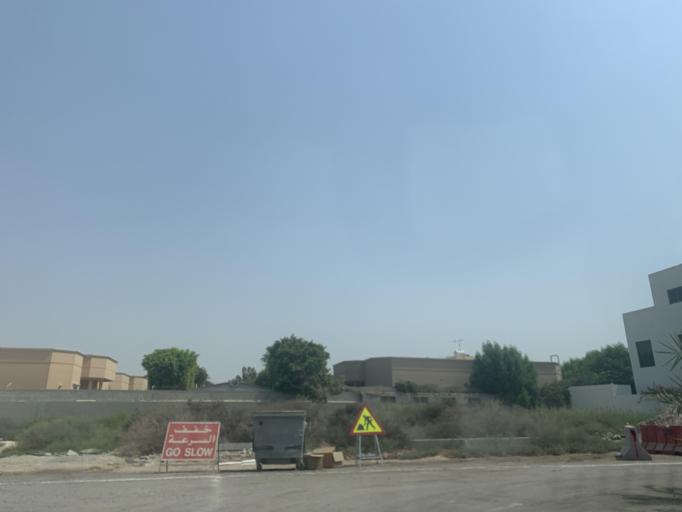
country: BH
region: Manama
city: Jidd Hafs
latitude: 26.1999
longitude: 50.4909
